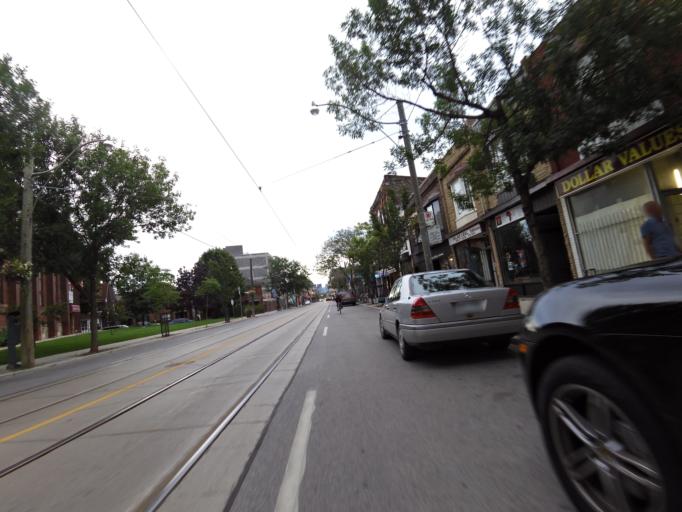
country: CA
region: Ontario
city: Toronto
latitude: 43.6500
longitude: -79.4377
